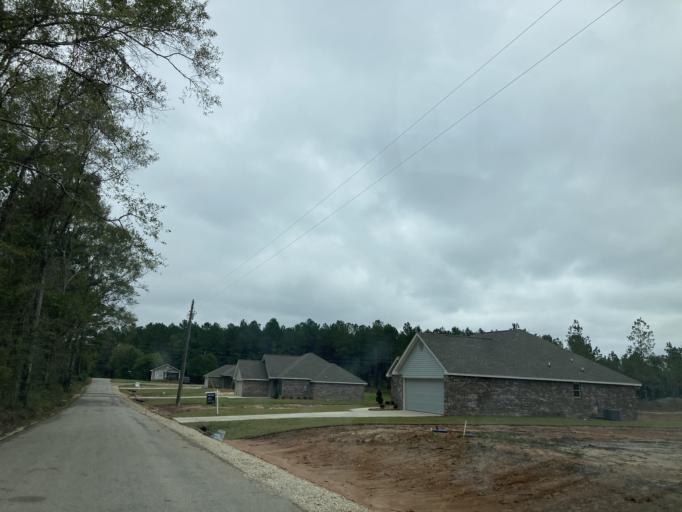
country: US
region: Mississippi
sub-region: Lamar County
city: Purvis
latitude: 31.1880
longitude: -89.4269
